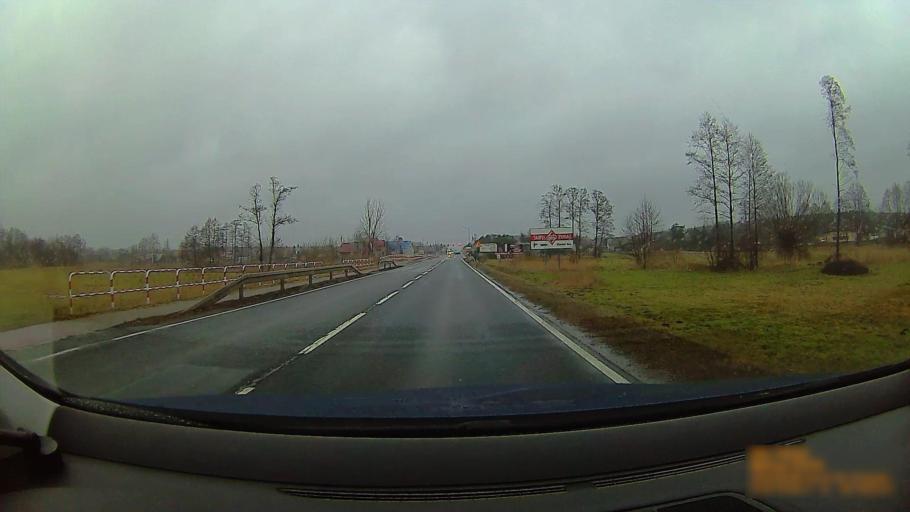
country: PL
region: Greater Poland Voivodeship
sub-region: Konin
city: Konin
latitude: 52.1737
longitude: 18.2726
